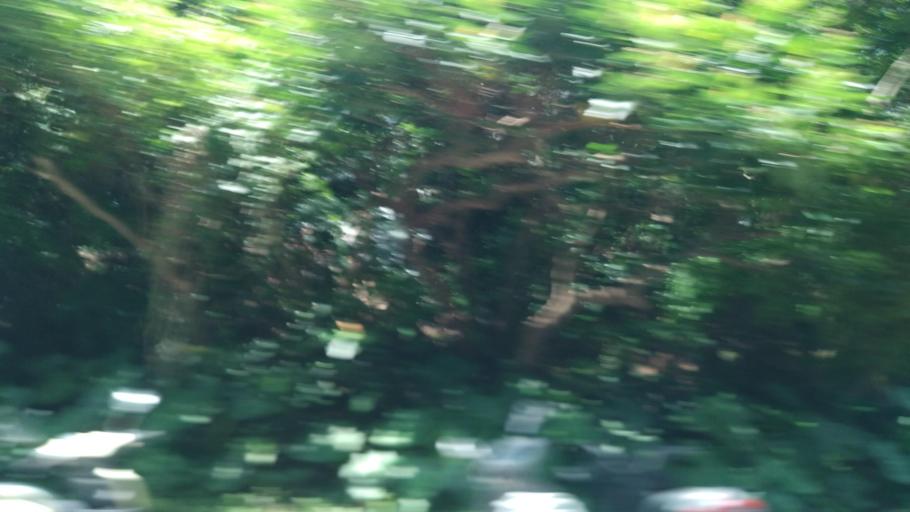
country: TW
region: Taipei
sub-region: Taipei
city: Banqiao
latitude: 24.9407
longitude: 121.5024
